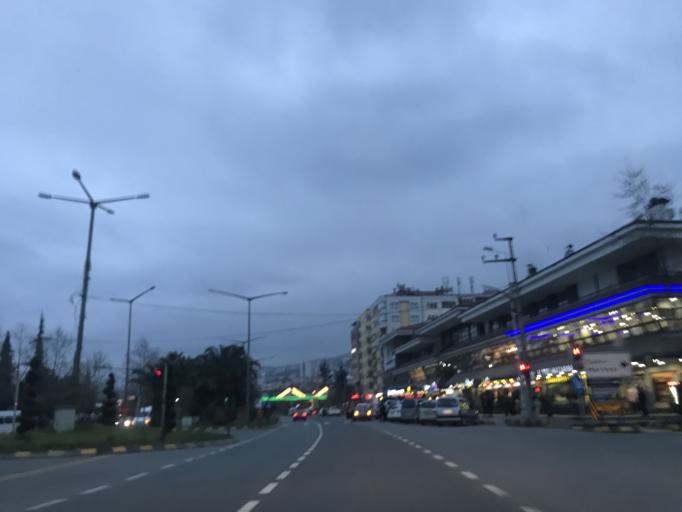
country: TR
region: Trabzon
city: Akcaabat
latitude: 41.0256
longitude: 39.5650
